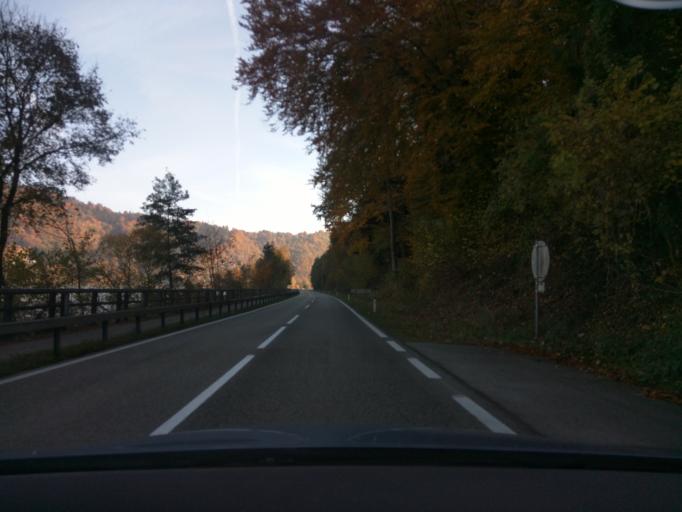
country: DE
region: Bavaria
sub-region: Lower Bavaria
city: Obernzell
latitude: 48.5505
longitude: 13.6417
